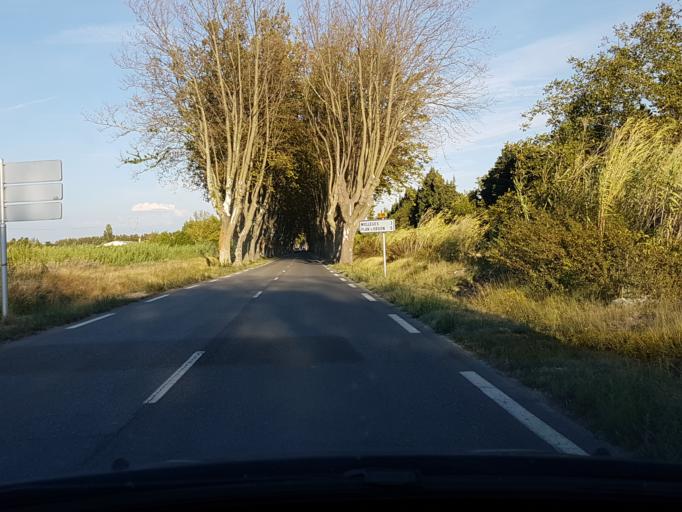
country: FR
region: Provence-Alpes-Cote d'Azur
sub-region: Departement des Bouches-du-Rhone
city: Molleges
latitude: 43.7865
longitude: 4.9404
